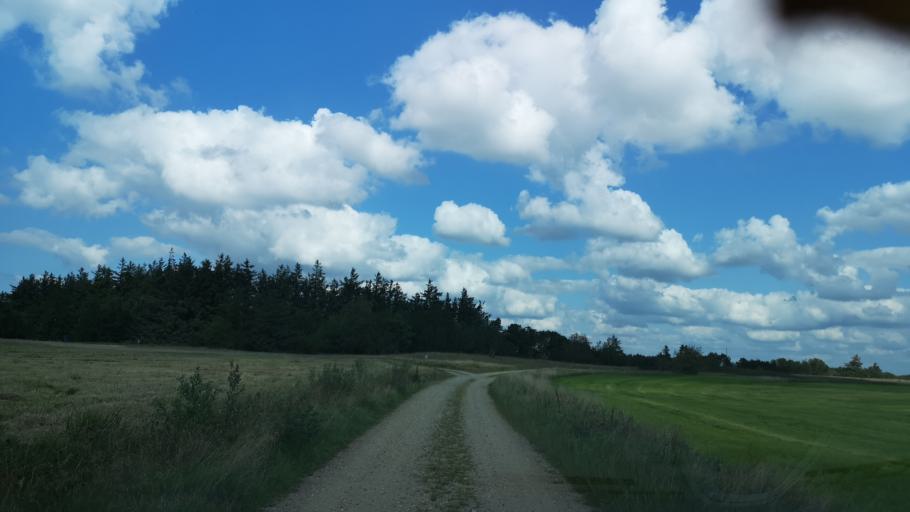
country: DK
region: Central Jutland
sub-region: Ringkobing-Skjern Kommune
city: Skjern
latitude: 55.8967
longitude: 8.3789
